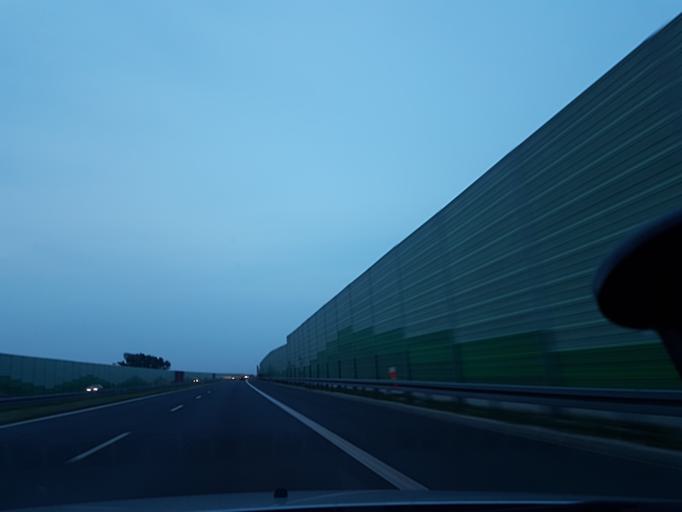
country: PL
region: Lodz Voivodeship
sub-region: Powiat leczycki
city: Piatek
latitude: 52.1180
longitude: 19.5023
